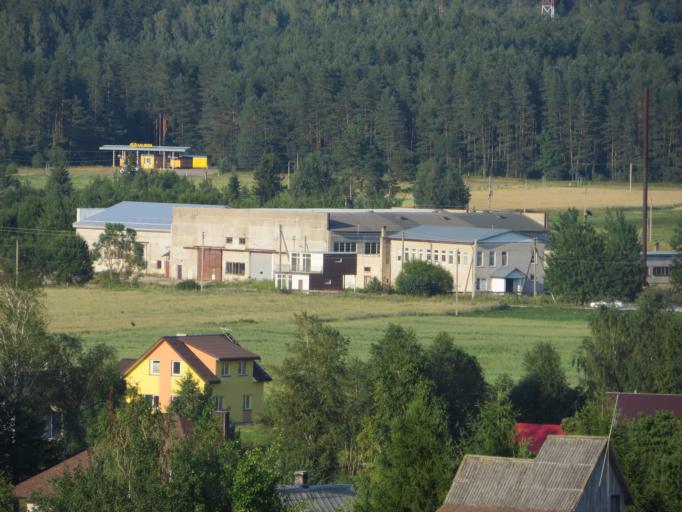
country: LT
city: Salcininkai
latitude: 54.4384
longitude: 25.3023
